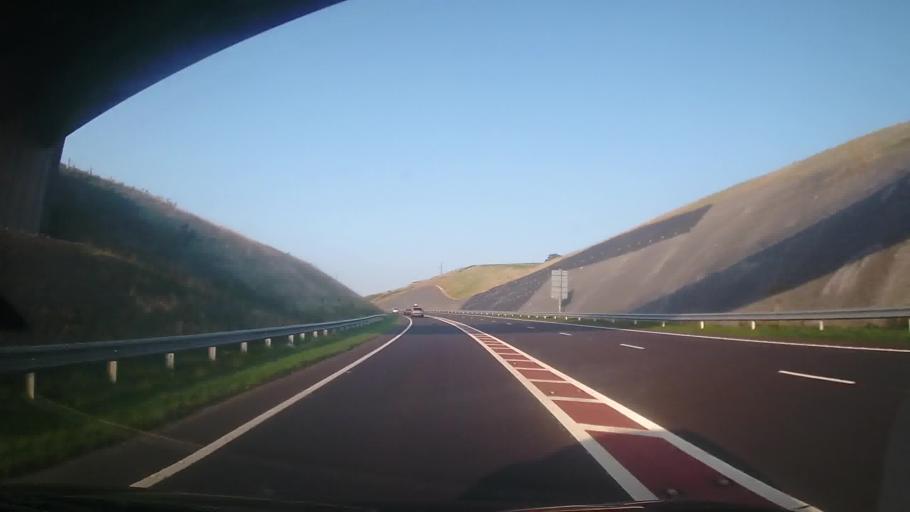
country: GB
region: Wales
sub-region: Sir Powys
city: Newtown
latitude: 52.5026
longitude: -3.3162
